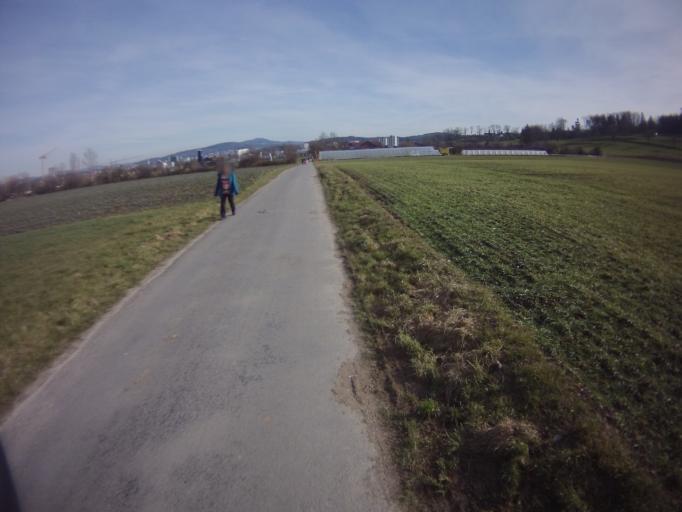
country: CH
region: Zurich
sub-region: Bezirk Dietikon
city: Dietikon / Almend
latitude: 47.4116
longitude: 8.3809
